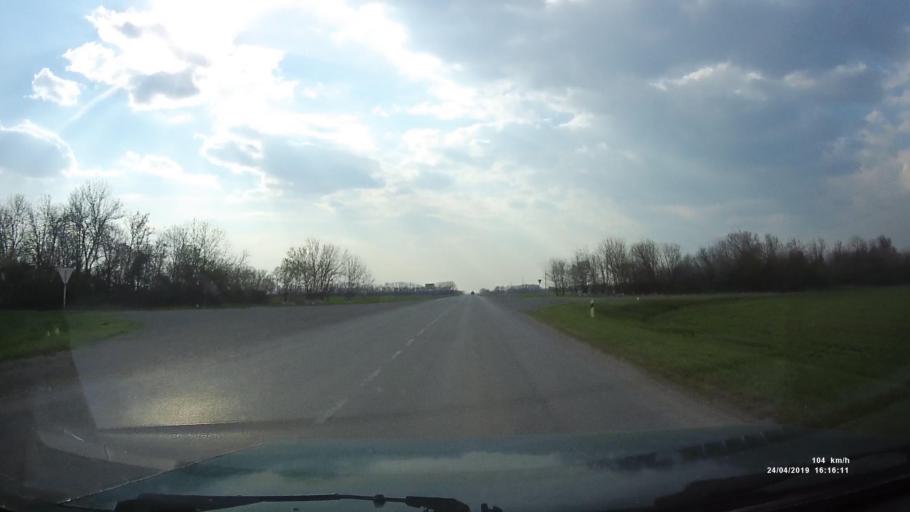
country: RU
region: Rostov
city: Sovetskoye
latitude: 46.7617
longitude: 42.1650
